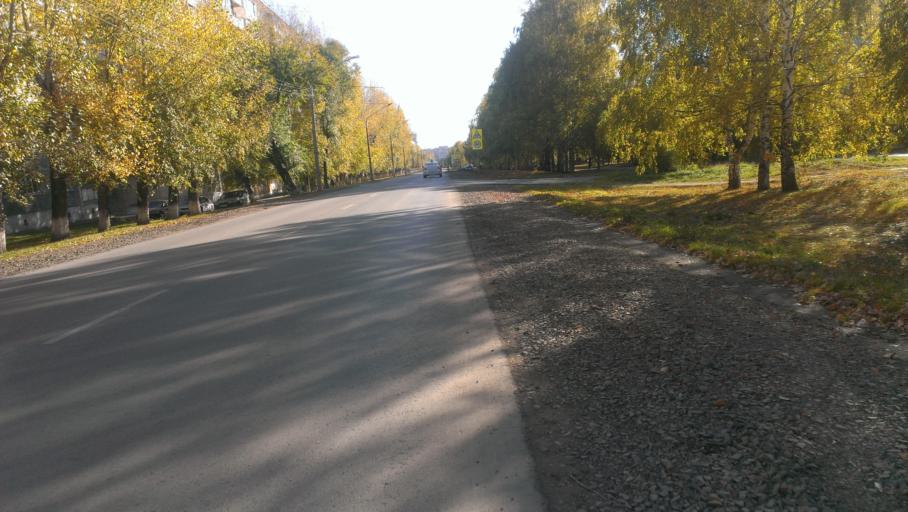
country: RU
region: Altai Krai
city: Novosilikatnyy
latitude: 53.3538
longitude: 83.6774
